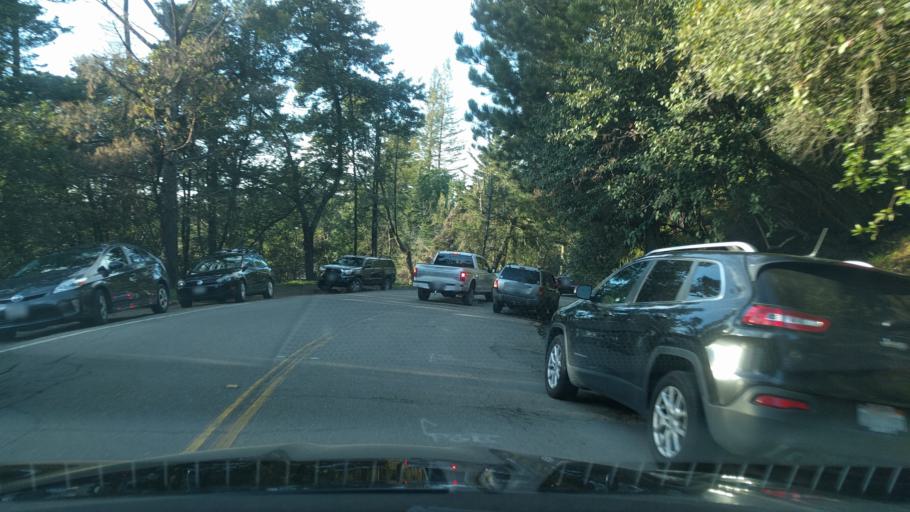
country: US
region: California
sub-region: Contra Costa County
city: Orinda
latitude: 37.8324
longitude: -122.1859
